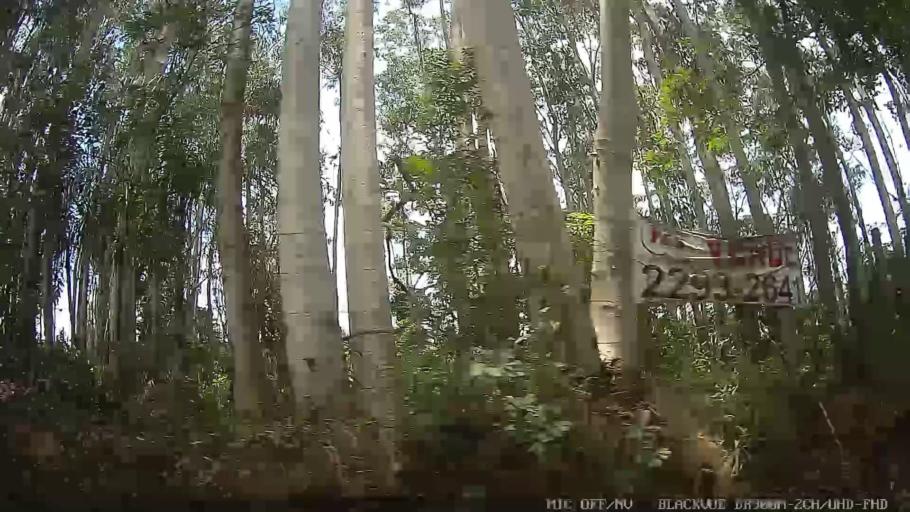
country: BR
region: Sao Paulo
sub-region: Atibaia
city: Atibaia
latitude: -23.0691
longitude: -46.6234
